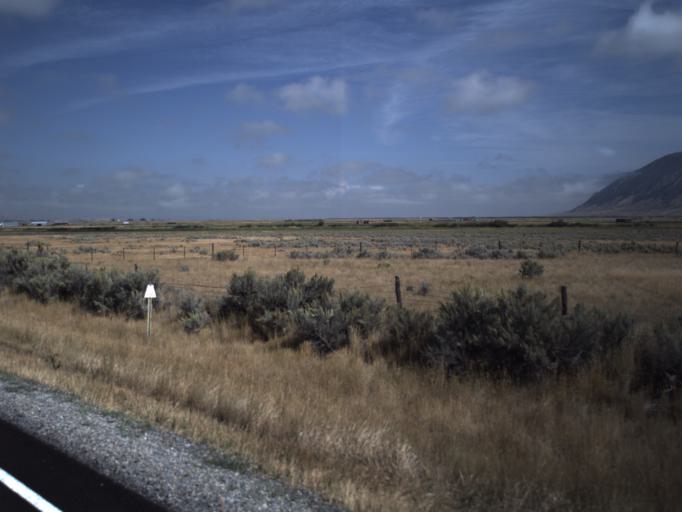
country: US
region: Utah
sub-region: Rich County
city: Randolph
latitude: 41.5877
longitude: -111.1695
